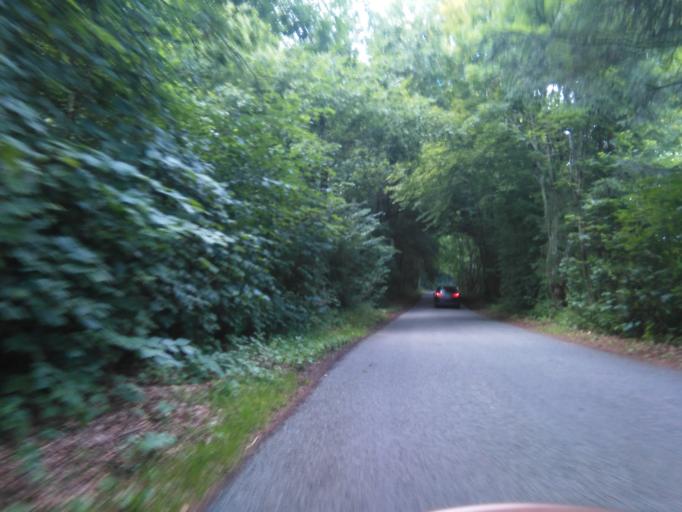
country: DK
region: Central Jutland
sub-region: Skanderborg Kommune
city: Horning
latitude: 56.1013
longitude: 10.0173
